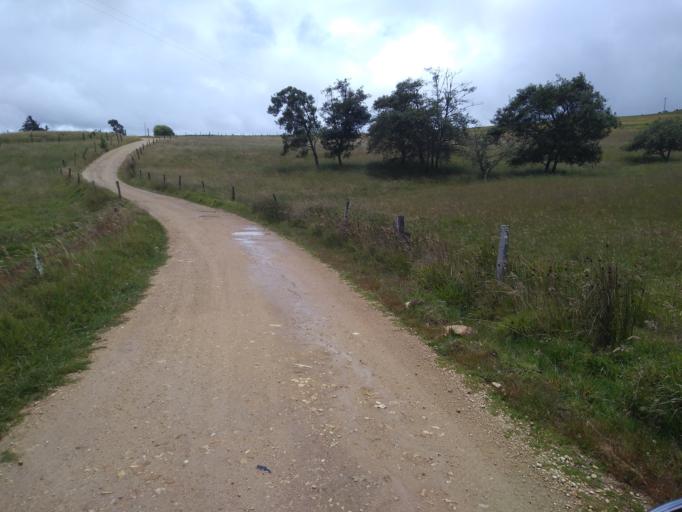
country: CO
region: Boyaca
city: Toca
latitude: 5.5872
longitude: -73.1399
